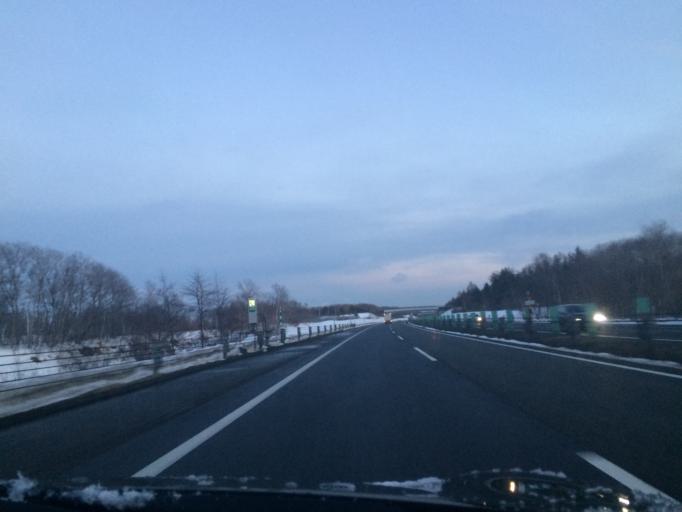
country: JP
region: Hokkaido
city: Chitose
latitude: 42.8296
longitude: 141.6128
